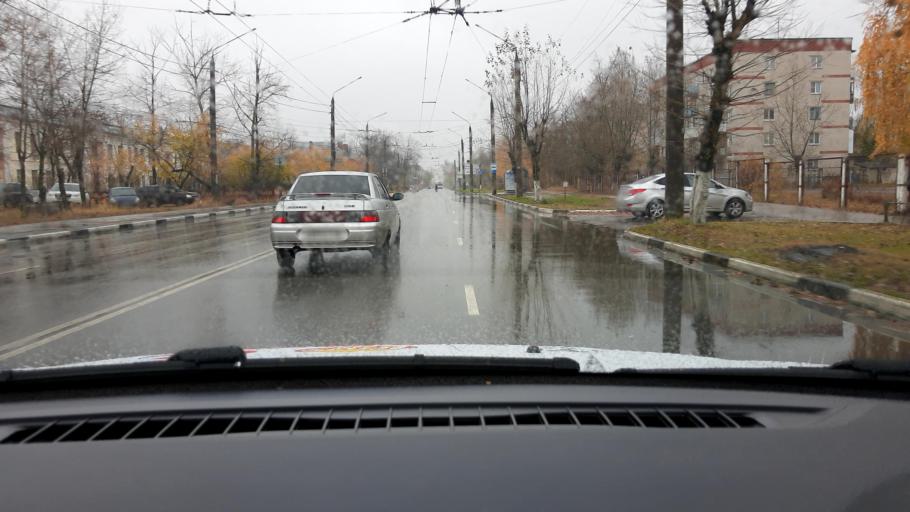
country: RU
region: Nizjnij Novgorod
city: Dzerzhinsk
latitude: 56.2429
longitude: 43.4727
